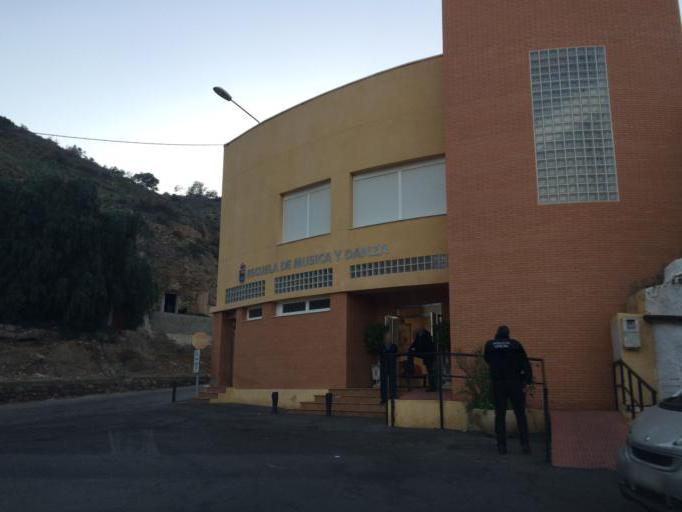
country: ES
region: Andalusia
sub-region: Provincia de Almeria
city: Gador
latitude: 36.9530
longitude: -2.4946
